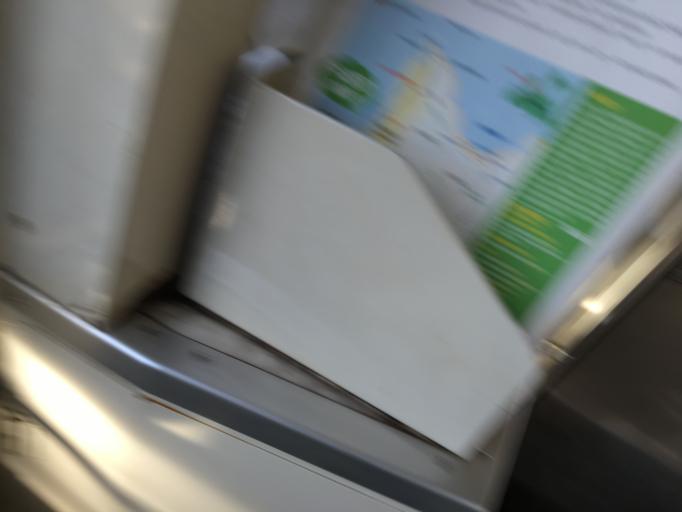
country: JP
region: Aomori
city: Goshogawara
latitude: 40.8098
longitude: 140.4486
